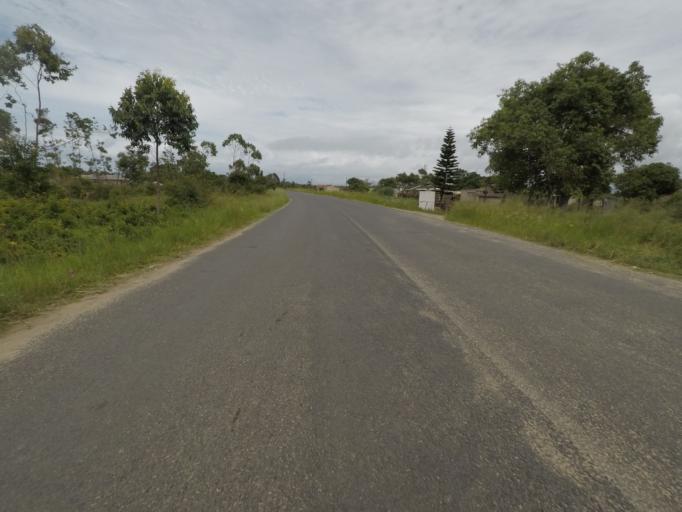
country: ZA
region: KwaZulu-Natal
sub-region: uThungulu District Municipality
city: eSikhawini
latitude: -28.9067
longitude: 31.8827
